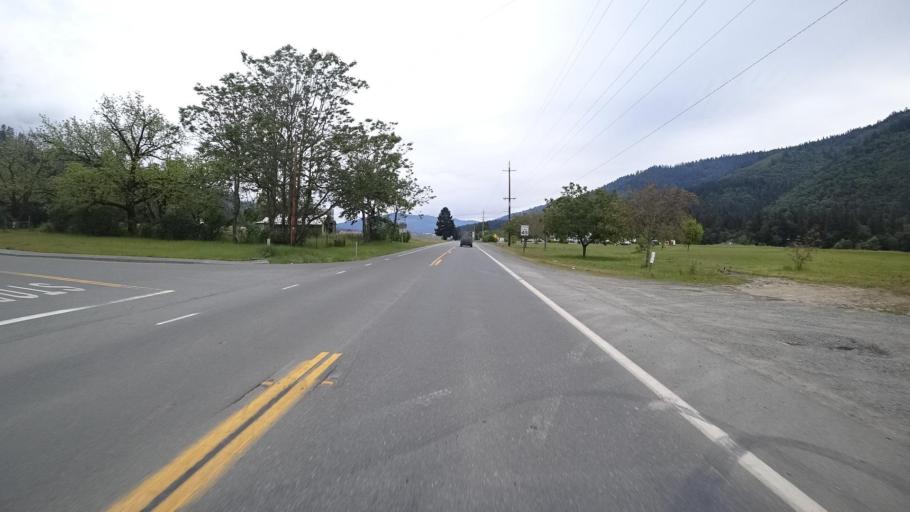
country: US
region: California
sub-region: Humboldt County
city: Willow Creek
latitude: 41.0453
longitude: -123.6727
